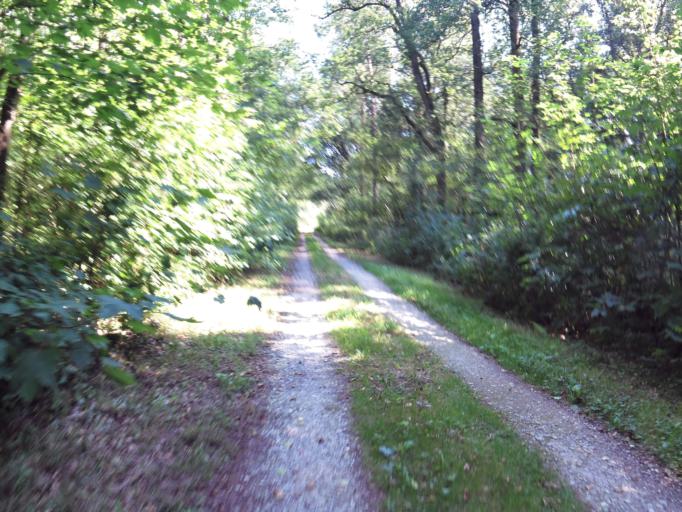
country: DE
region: North Rhine-Westphalia
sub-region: Regierungsbezirk Munster
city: Telgte
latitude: 51.9620
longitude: 7.7509
